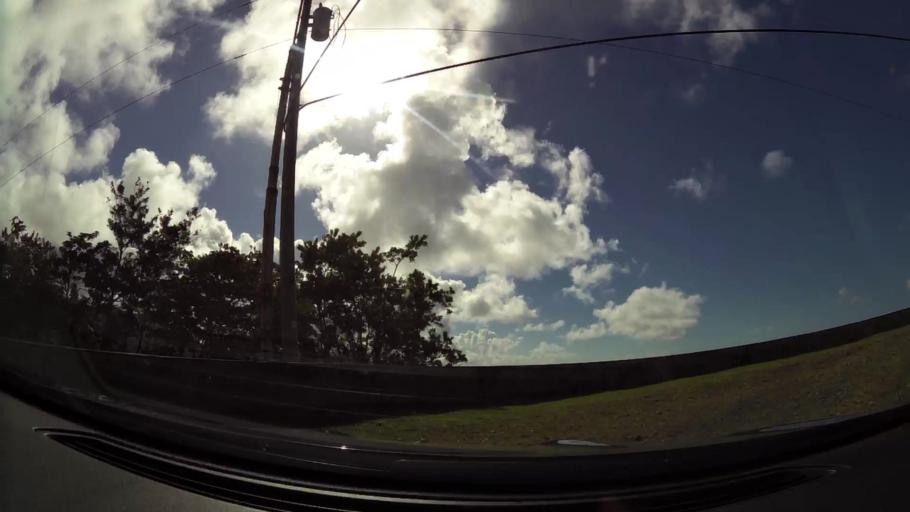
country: TT
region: Eastern Tobago
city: Roxborough
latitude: 11.3293
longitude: -60.5399
